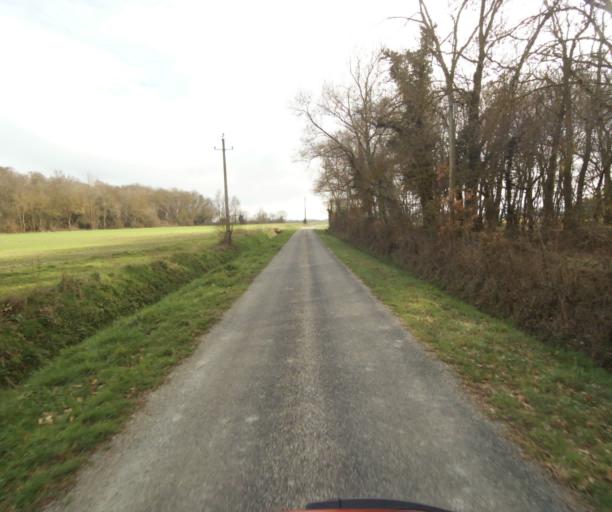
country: FR
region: Midi-Pyrenees
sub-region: Departement de l'Ariege
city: Mazeres
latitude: 43.2065
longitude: 1.6803
